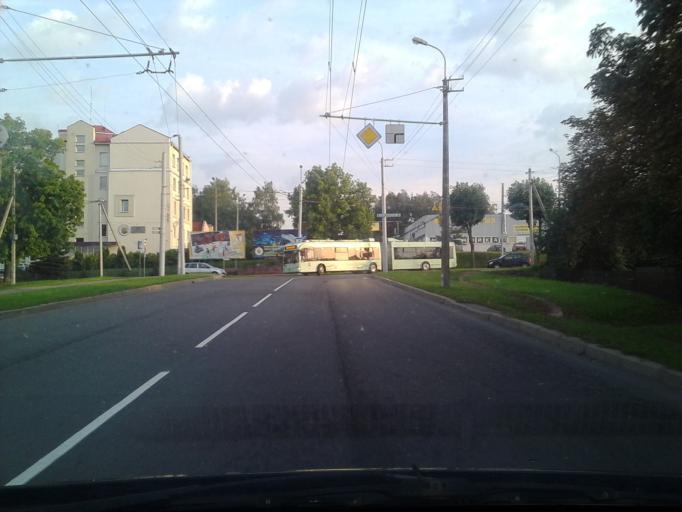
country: BY
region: Minsk
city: Minsk
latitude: 53.9514
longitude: 27.5968
